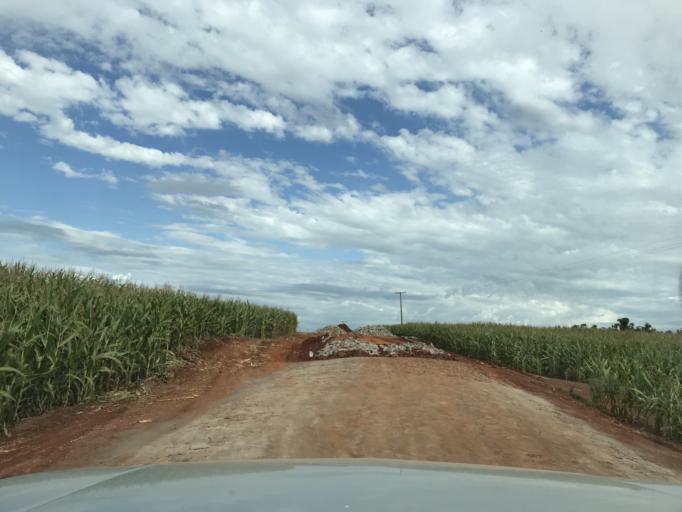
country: BR
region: Parana
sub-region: Palotina
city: Palotina
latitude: -24.3045
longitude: -53.8089
